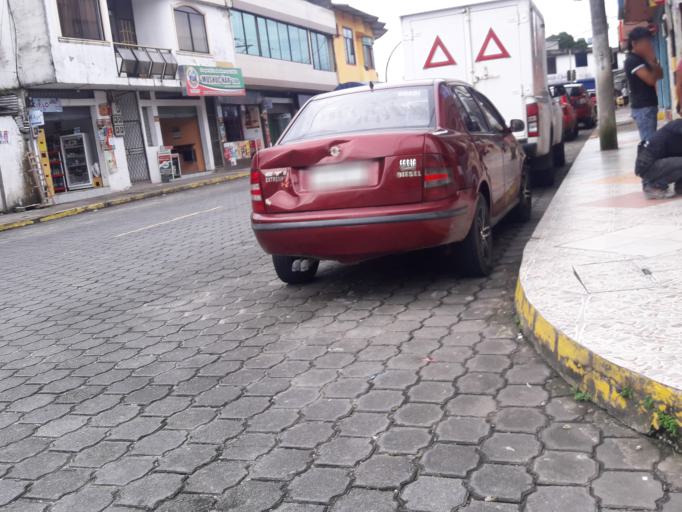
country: EC
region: Napo
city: Tena
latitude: -0.9980
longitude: -77.8134
